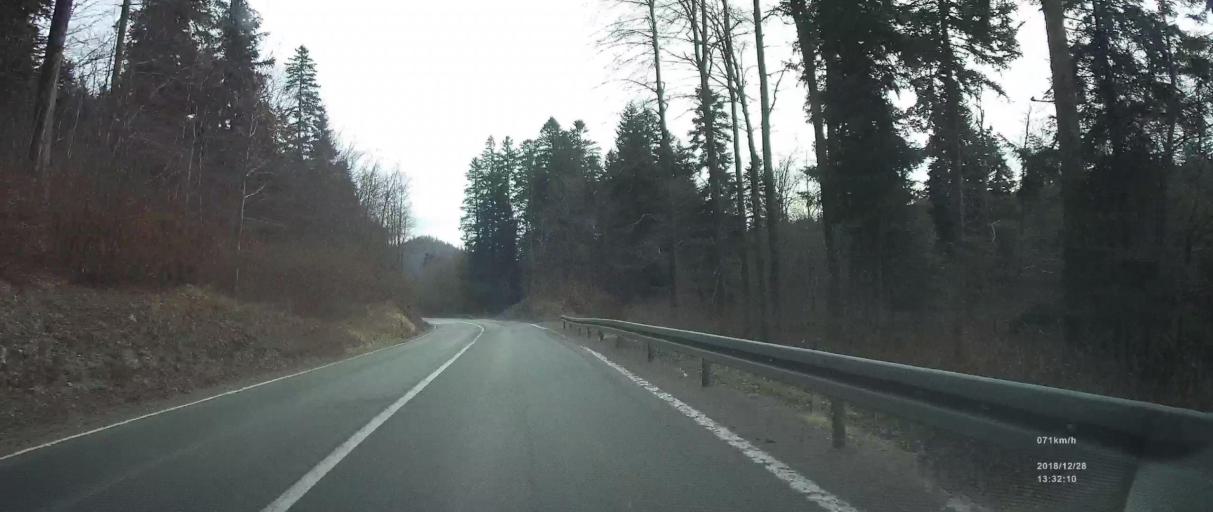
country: HR
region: Primorsko-Goranska
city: Hreljin
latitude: 45.3482
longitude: 14.6611
